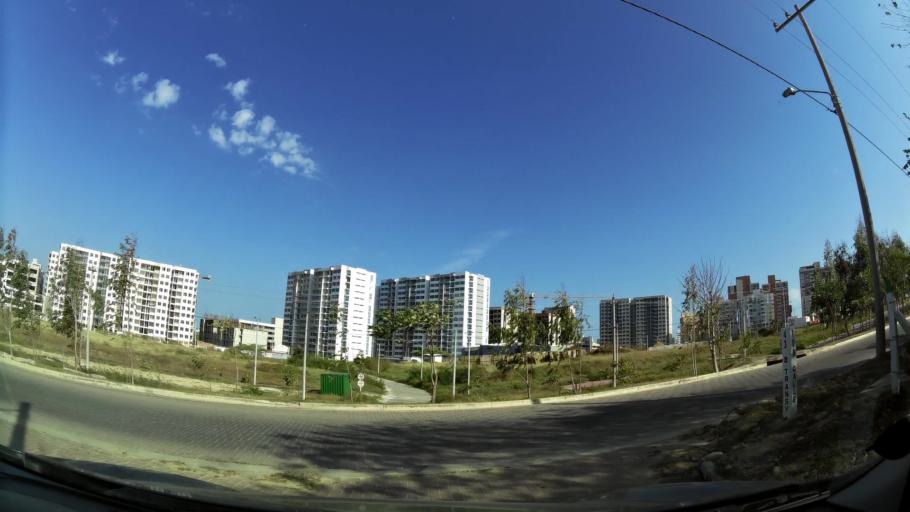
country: CO
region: Atlantico
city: Barranquilla
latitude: 11.0053
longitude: -74.8370
